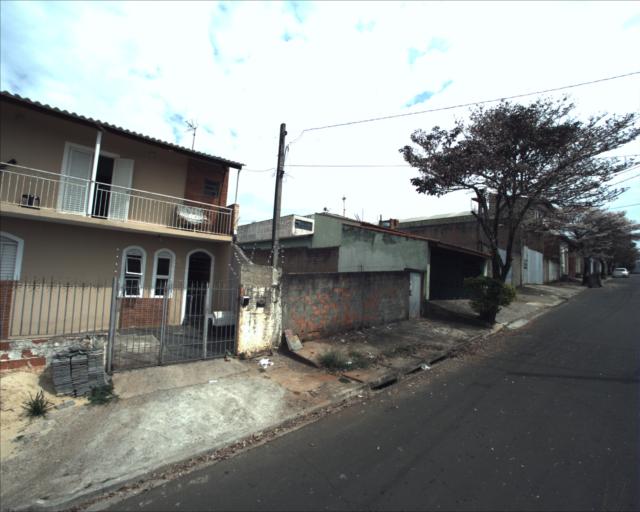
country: BR
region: Sao Paulo
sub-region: Sorocaba
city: Sorocaba
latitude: -23.5022
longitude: -47.5228
